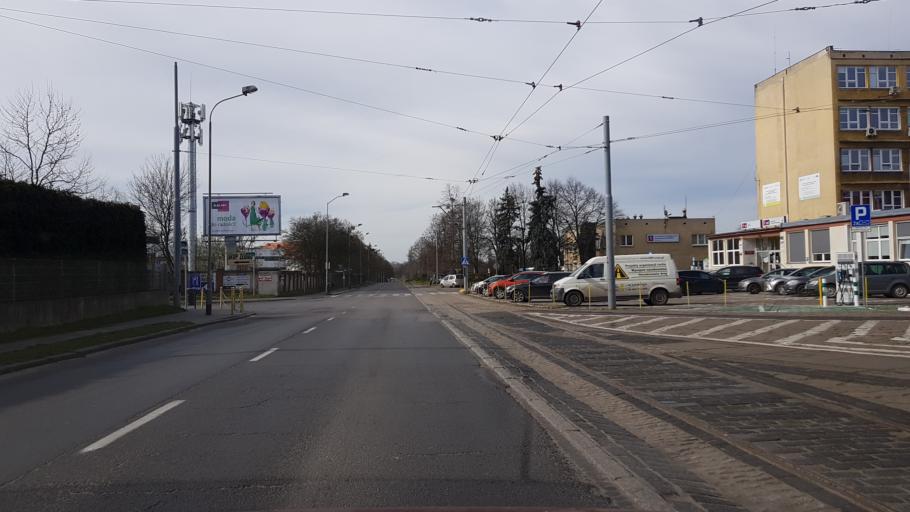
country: PL
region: West Pomeranian Voivodeship
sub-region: Szczecin
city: Szczecin
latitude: 53.4501
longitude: 14.4970
